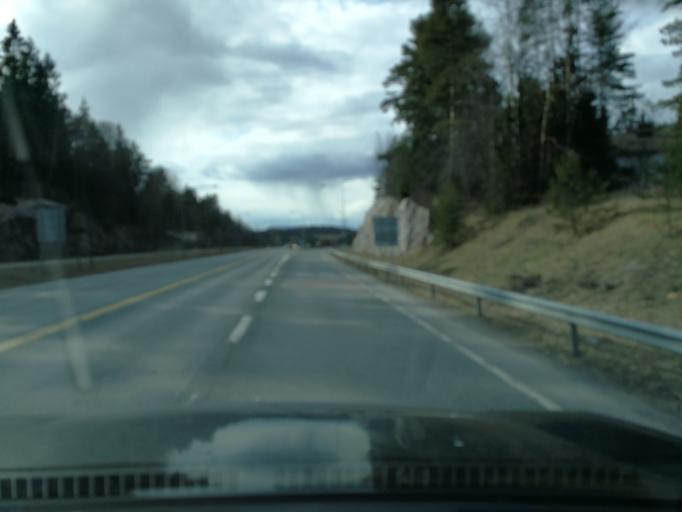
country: FI
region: Varsinais-Suomi
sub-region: Turku
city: Kaarina
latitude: 60.4690
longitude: 22.3731
